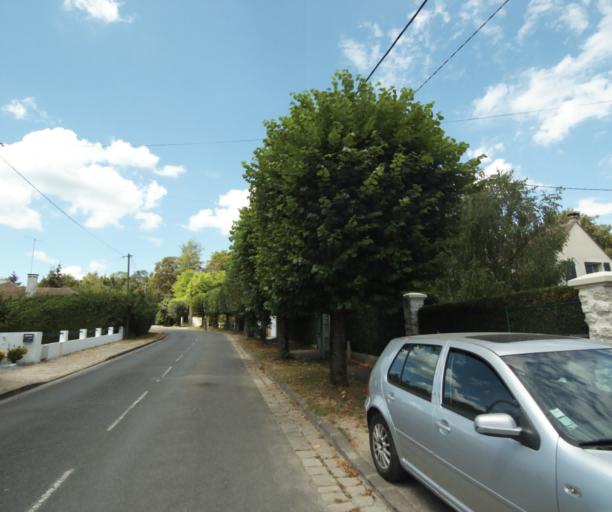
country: FR
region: Ile-de-France
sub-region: Departement de Seine-et-Marne
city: Hericy
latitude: 48.4546
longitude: 2.7593
